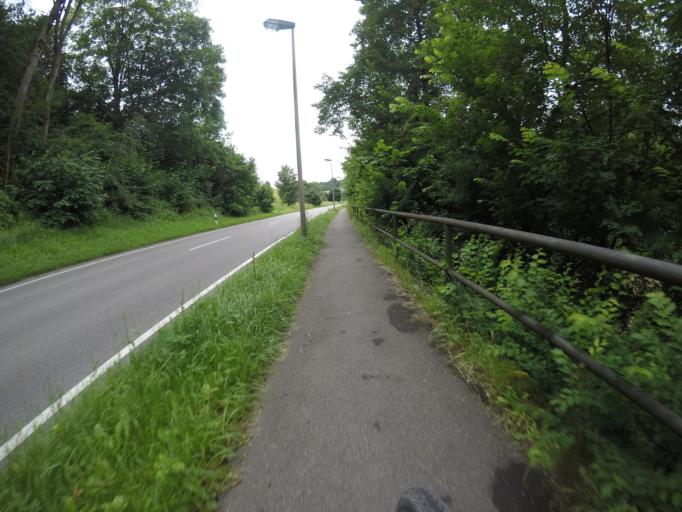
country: DE
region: Baden-Wuerttemberg
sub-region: Regierungsbezirk Stuttgart
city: Reichenbach an der Fils
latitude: 48.7066
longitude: 9.4606
